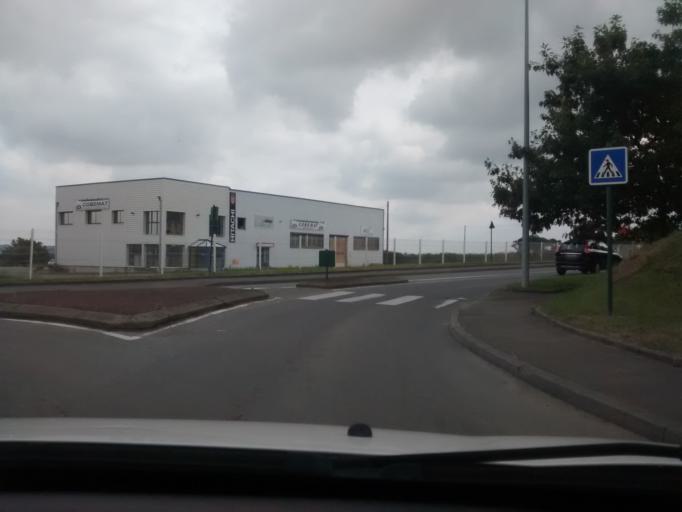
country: FR
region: Brittany
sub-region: Departement d'Ille-et-Vilaine
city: Cesson-Sevigne
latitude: 48.1161
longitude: -1.5817
